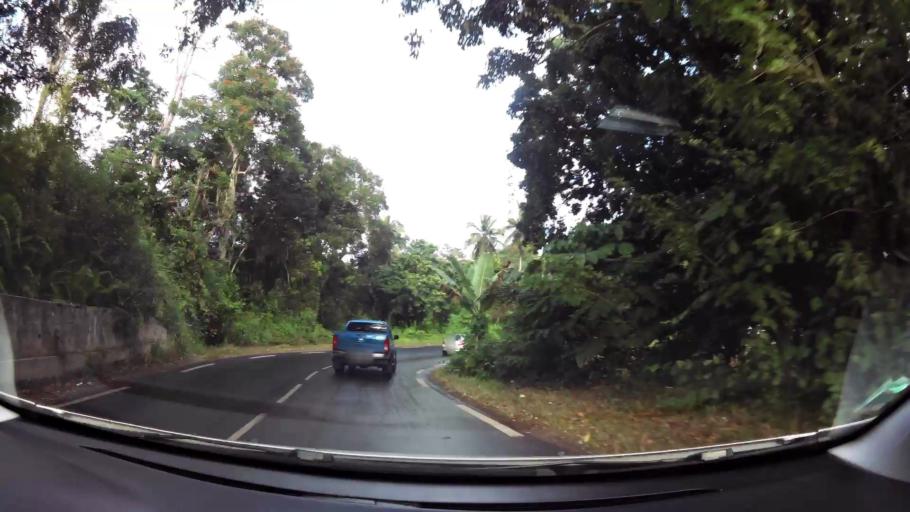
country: YT
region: Ouangani
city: Ouangani
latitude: -12.8365
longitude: 45.1435
